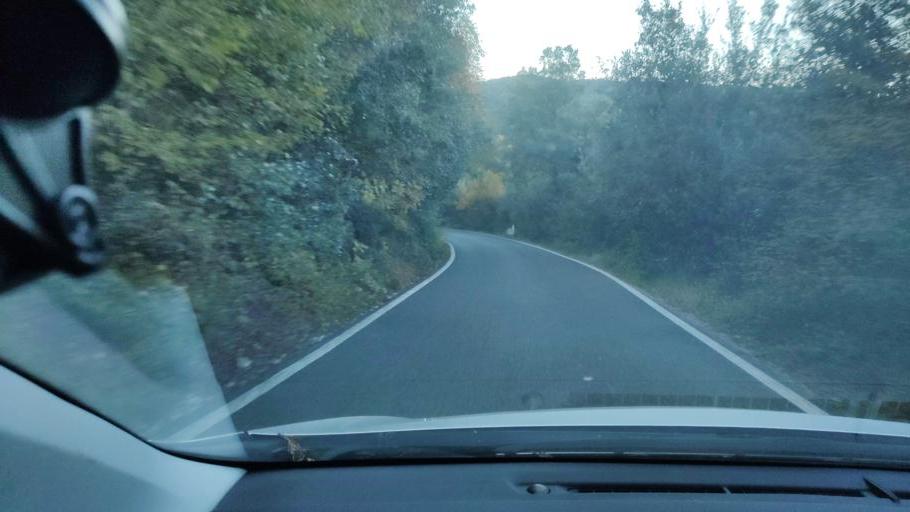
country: IT
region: Umbria
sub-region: Provincia di Terni
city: Amelia
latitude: 42.5861
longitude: 12.4317
